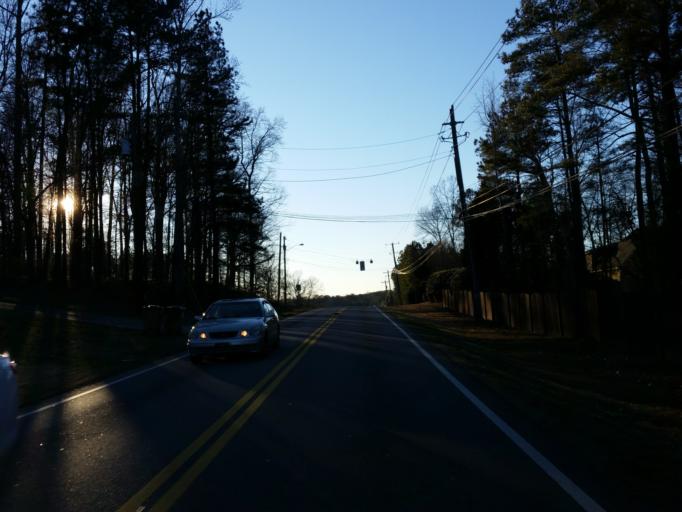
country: US
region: Georgia
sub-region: Cherokee County
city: Woodstock
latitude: 34.1309
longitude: -84.4907
